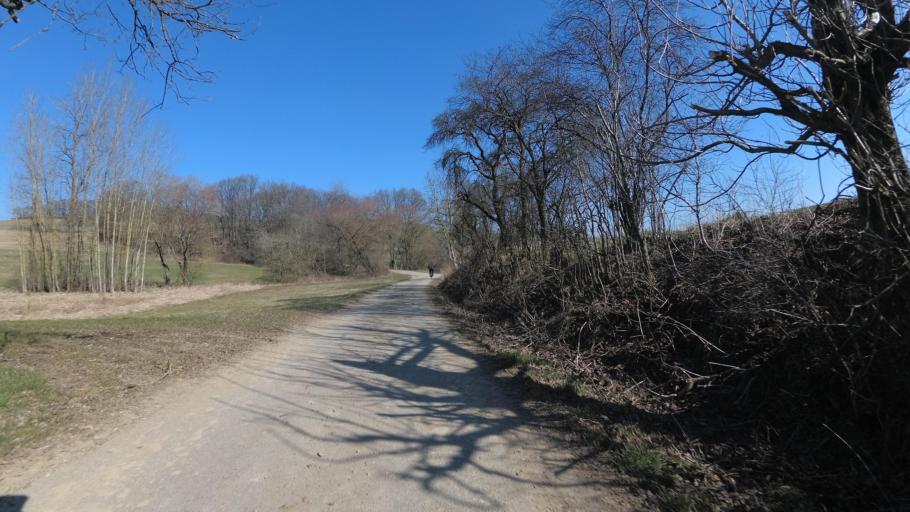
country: DE
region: Rheinland-Pfalz
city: Albessen
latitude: 49.5228
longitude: 7.3382
